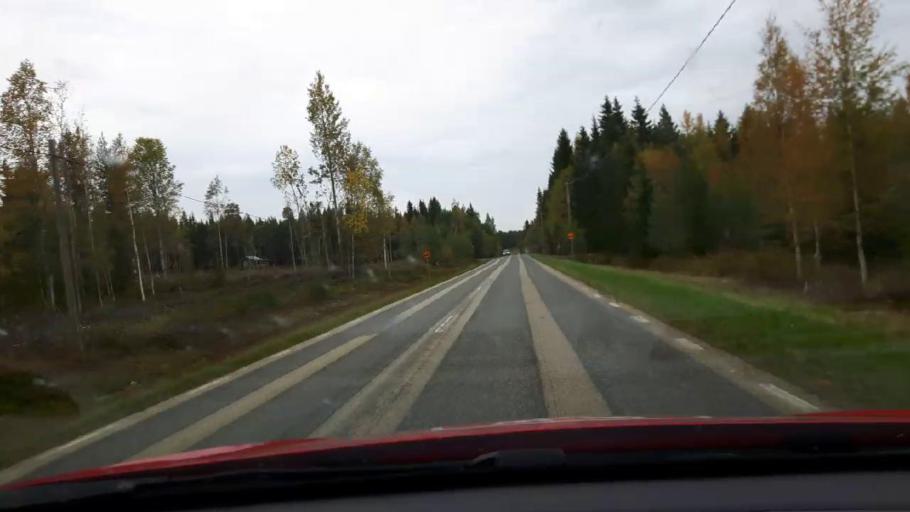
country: SE
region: Jaemtland
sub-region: Bergs Kommun
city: Hoverberg
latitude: 62.8697
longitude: 14.3716
